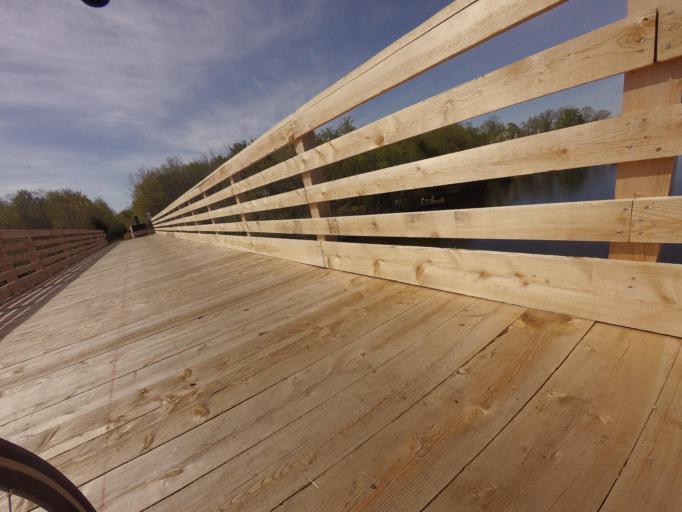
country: CA
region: Ontario
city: Arnprior
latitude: 45.4647
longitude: -76.2854
